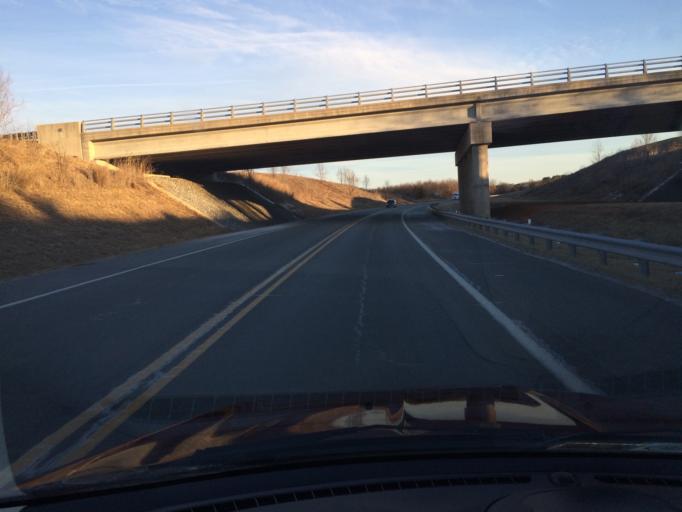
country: US
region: Virginia
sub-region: City of Staunton
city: Staunton
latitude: 38.1509
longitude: -79.1175
